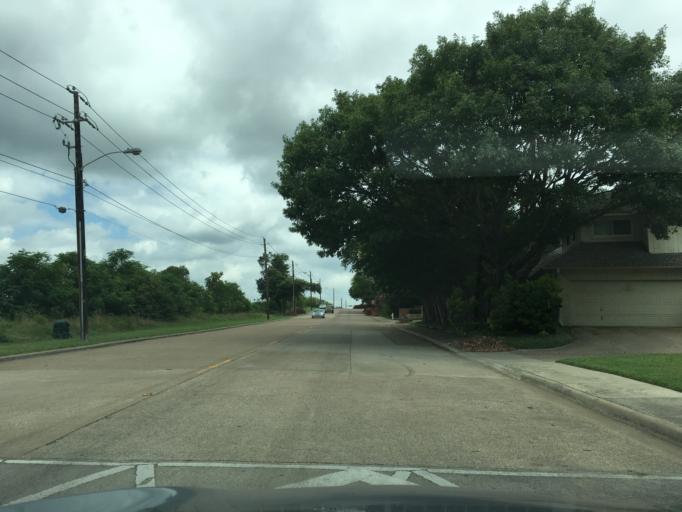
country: US
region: Texas
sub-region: Dallas County
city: Richardson
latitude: 32.8910
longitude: -96.7466
